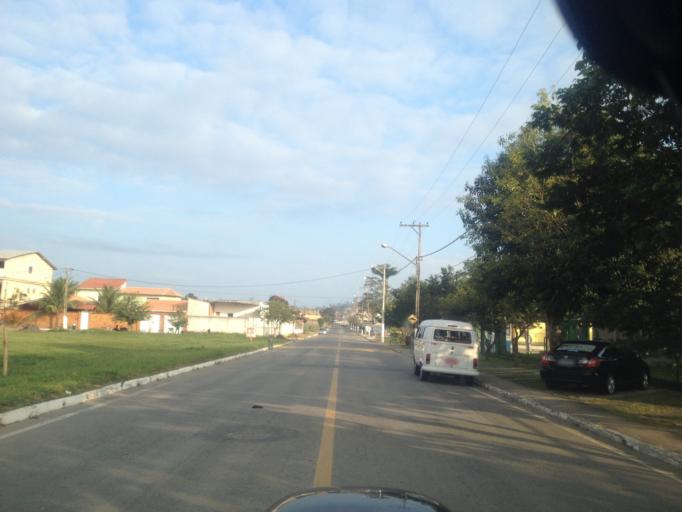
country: BR
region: Rio de Janeiro
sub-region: Porto Real
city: Porto Real
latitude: -22.4460
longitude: -44.3051
